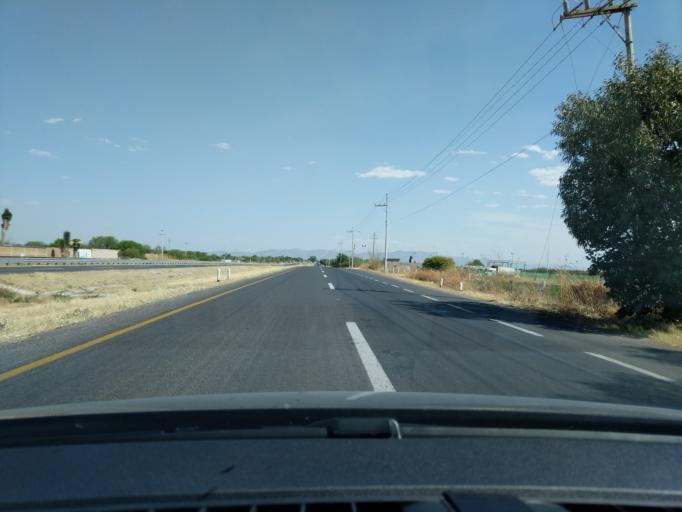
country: MX
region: Durango
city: Victoria de Durango
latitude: 24.0802
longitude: -104.5549
